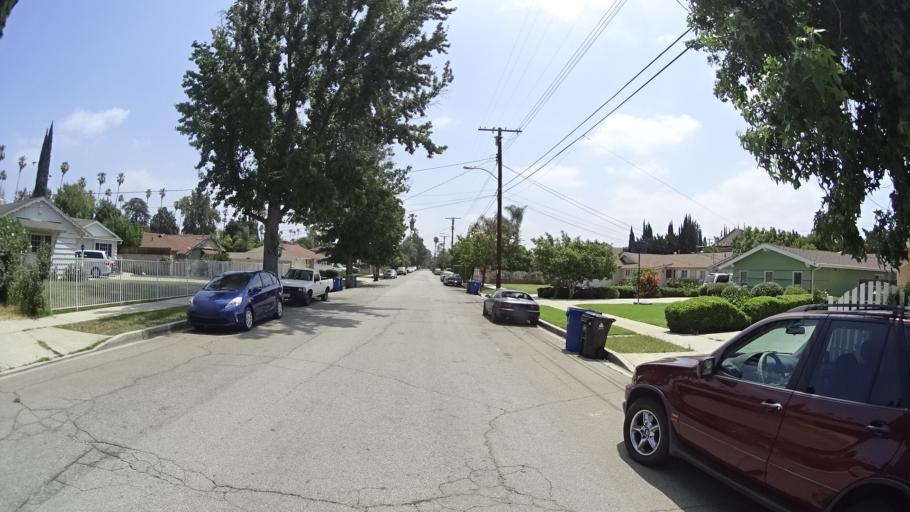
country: US
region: California
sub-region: Los Angeles County
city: Van Nuys
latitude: 34.1876
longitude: -118.4616
